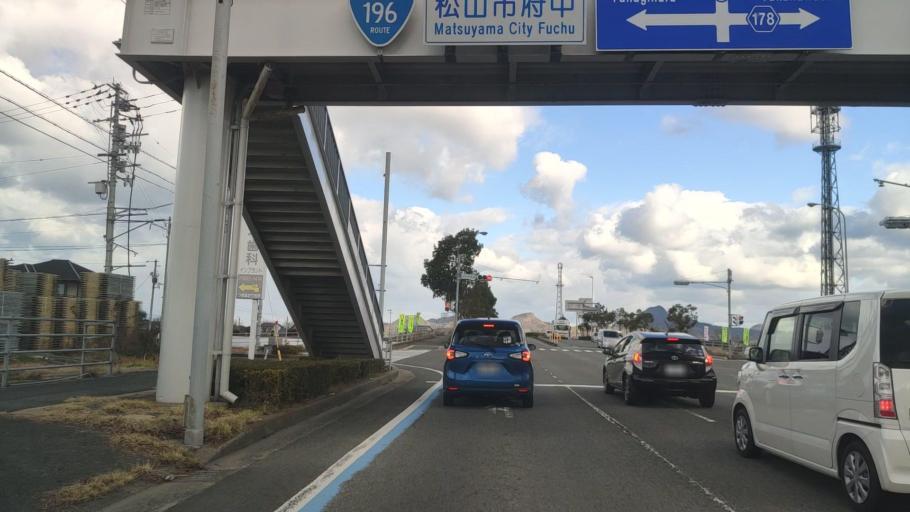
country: JP
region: Ehime
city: Hojo
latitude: 33.9532
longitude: 132.7752
